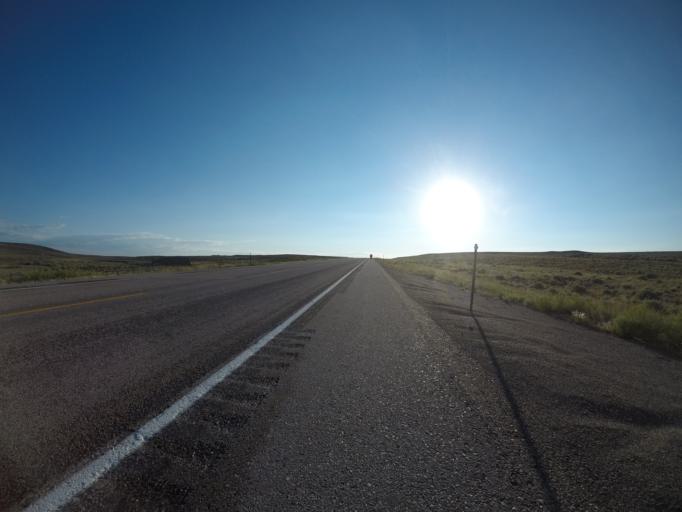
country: US
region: Wyoming
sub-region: Lincoln County
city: Kemmerer
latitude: 41.8745
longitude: -110.4472
